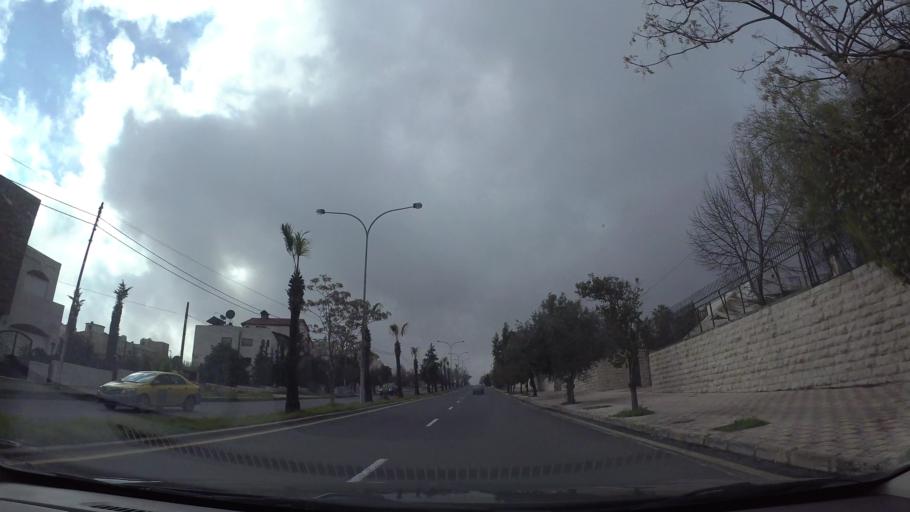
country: JO
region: Amman
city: Al Bunayyat ash Shamaliyah
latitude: 31.9510
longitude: 35.8863
